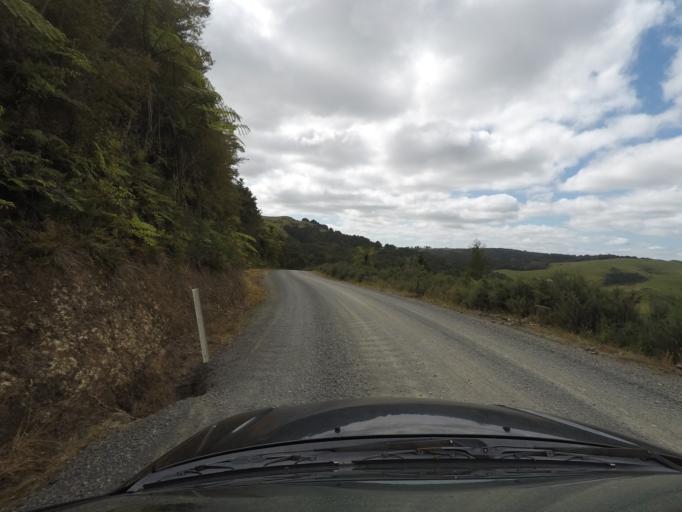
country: NZ
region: Northland
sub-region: Whangarei
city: Ruakaka
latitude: -35.9302
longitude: 174.3440
